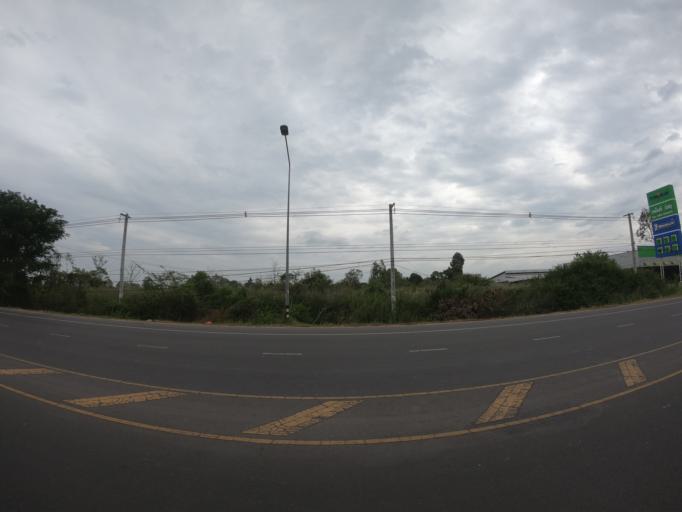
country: TH
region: Roi Et
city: Roi Et
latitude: 16.0704
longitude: 103.6792
